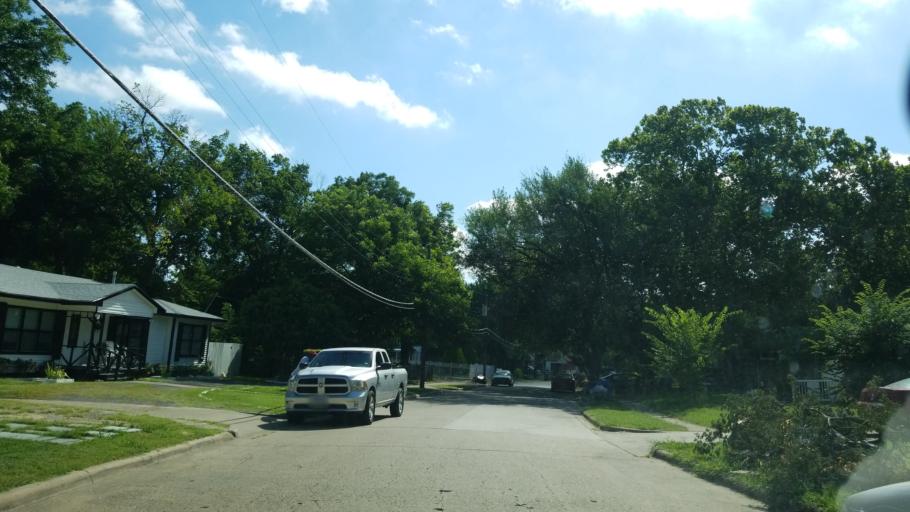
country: US
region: Texas
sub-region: Dallas County
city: Dallas
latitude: 32.7132
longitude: -96.7906
